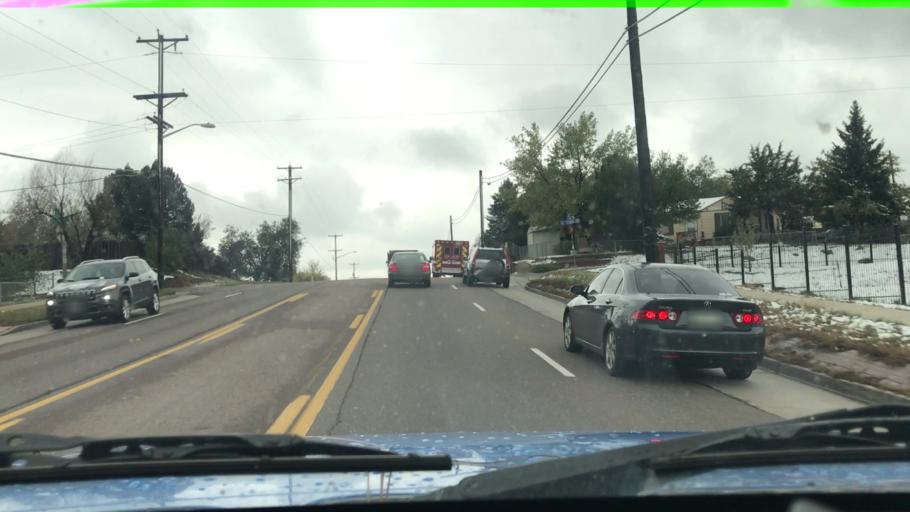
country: US
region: Colorado
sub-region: Jefferson County
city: Lakewood
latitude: 39.7081
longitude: -105.0533
